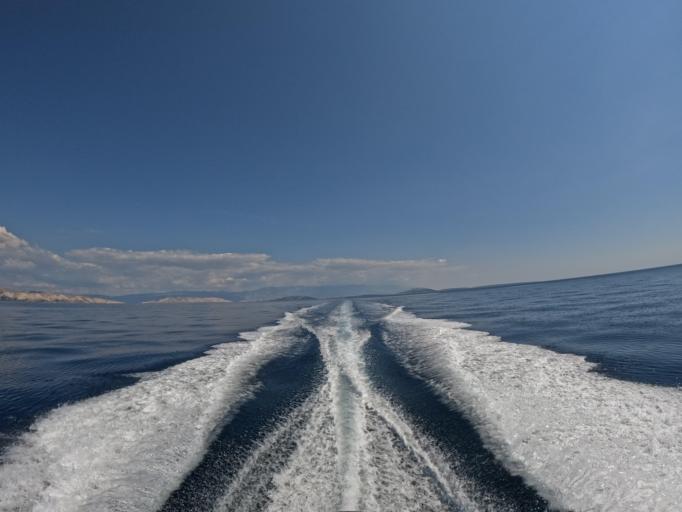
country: HR
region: Primorsko-Goranska
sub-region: Grad Krk
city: Krk
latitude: 44.9154
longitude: 14.5791
